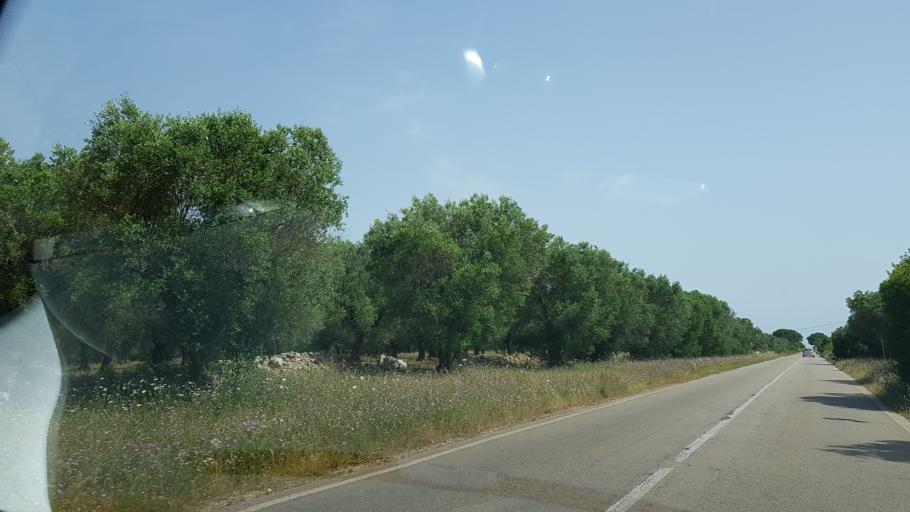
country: IT
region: Apulia
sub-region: Provincia di Brindisi
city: San Pancrazio Salentino
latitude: 40.3491
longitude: 17.8462
